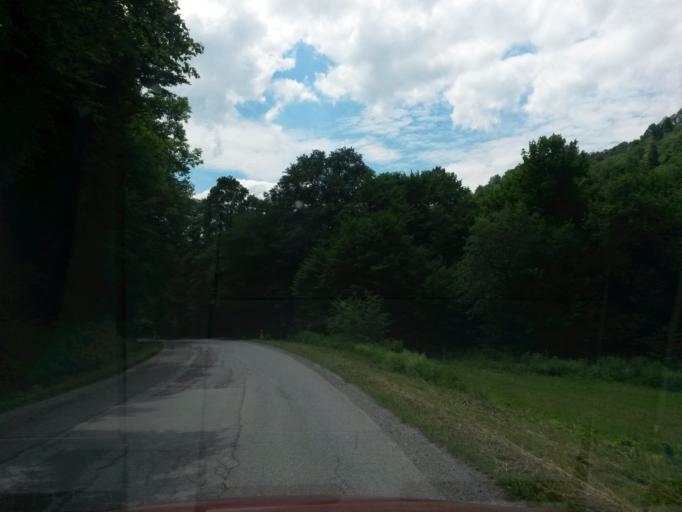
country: SK
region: Kosicky
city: Gelnica
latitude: 48.9130
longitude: 21.0301
